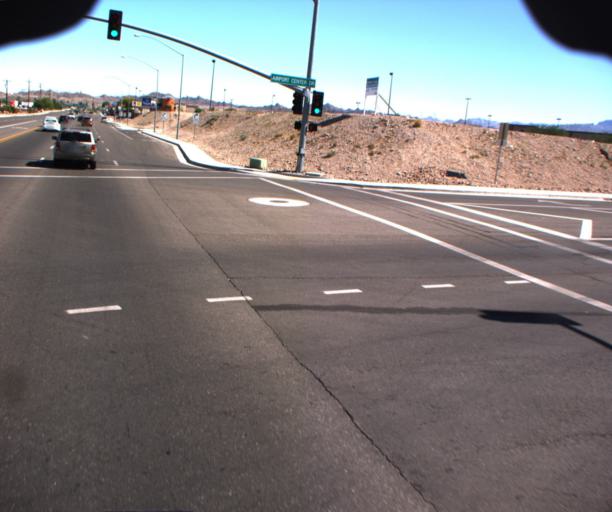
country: US
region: Nevada
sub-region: Clark County
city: Laughlin
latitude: 35.1648
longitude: -114.5663
